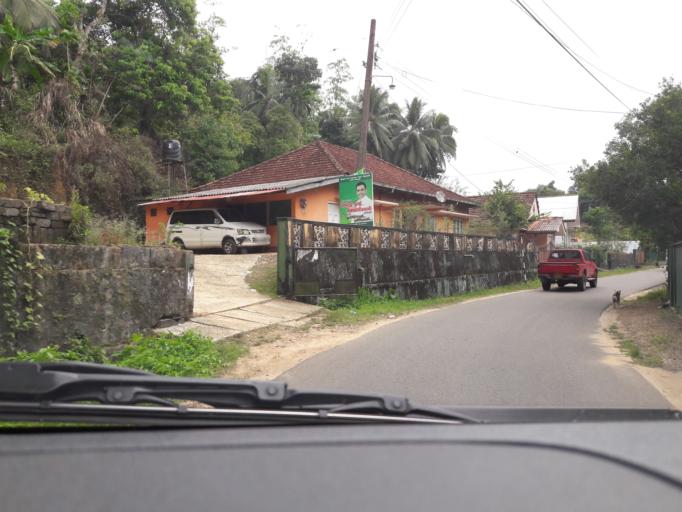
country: LK
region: Southern
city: Galle
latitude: 6.1824
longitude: 80.2993
